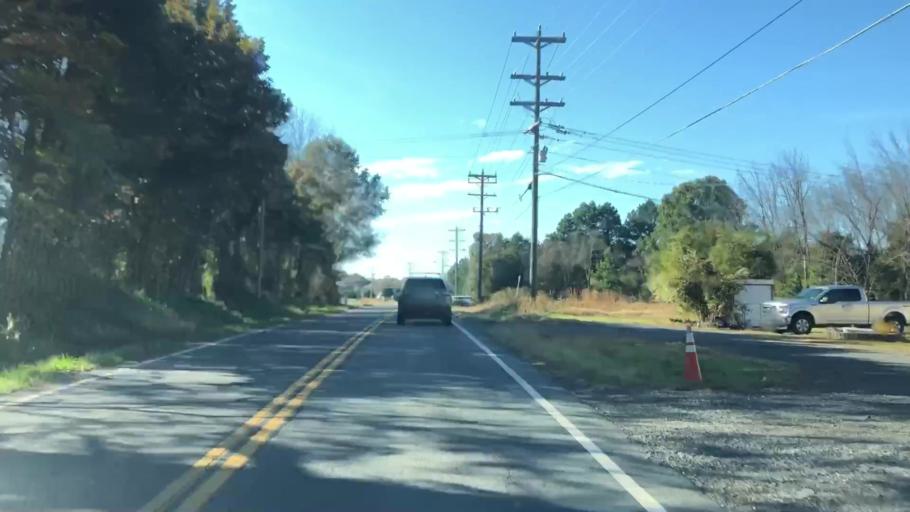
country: US
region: Virginia
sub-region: Prince William County
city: Gainesville
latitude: 38.7531
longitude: -77.6351
